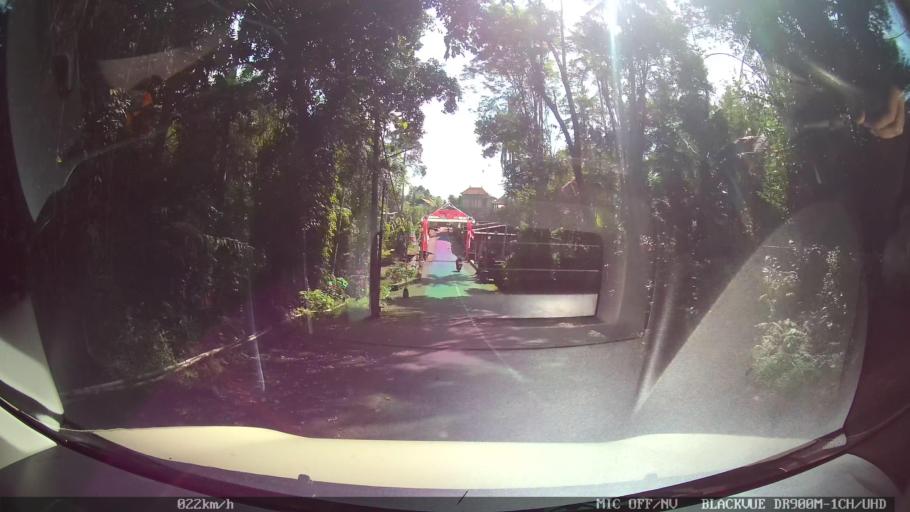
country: ID
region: Bali
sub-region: Kabupaten Gianyar
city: Ubud
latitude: -8.5113
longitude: 115.2890
